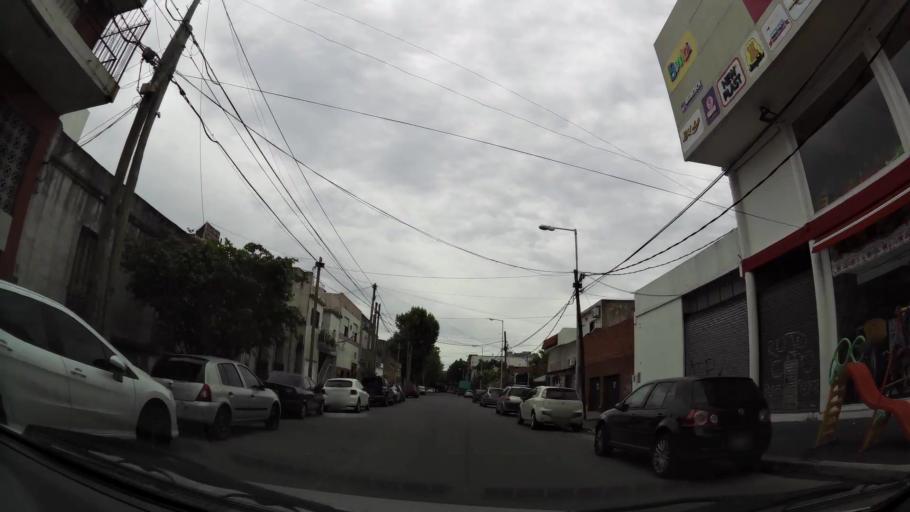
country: AR
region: Buenos Aires
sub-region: Partido de Avellaneda
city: Avellaneda
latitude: -34.6754
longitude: -58.3845
